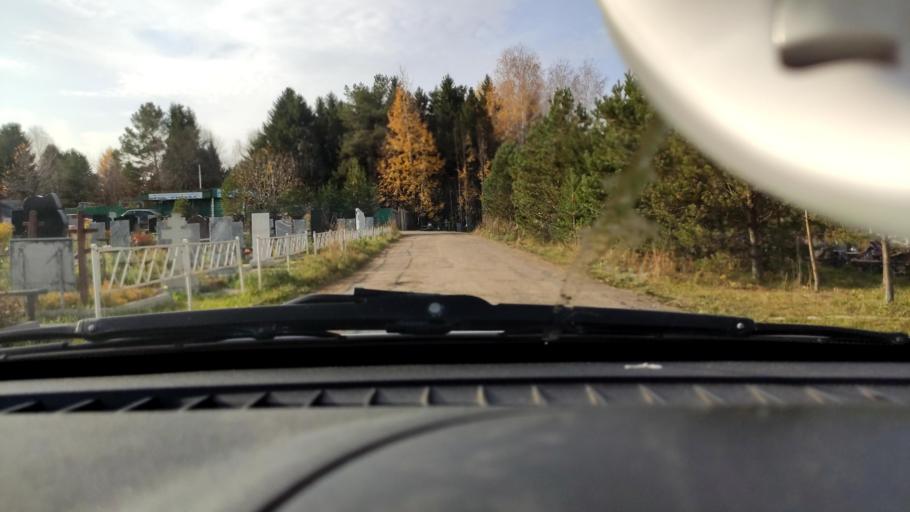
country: RU
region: Perm
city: Kultayevo
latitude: 57.8593
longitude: 55.8694
